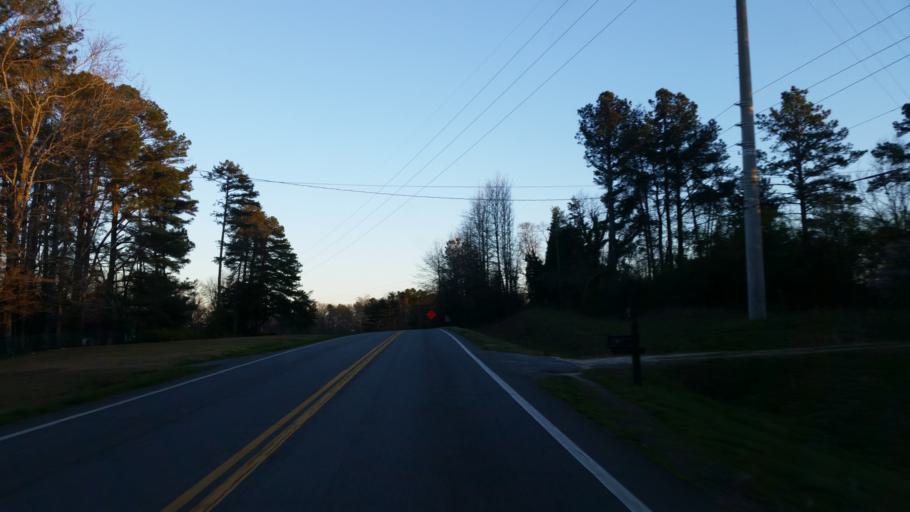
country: US
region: Georgia
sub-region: Hall County
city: Oakwood
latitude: 34.3154
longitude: -83.9994
